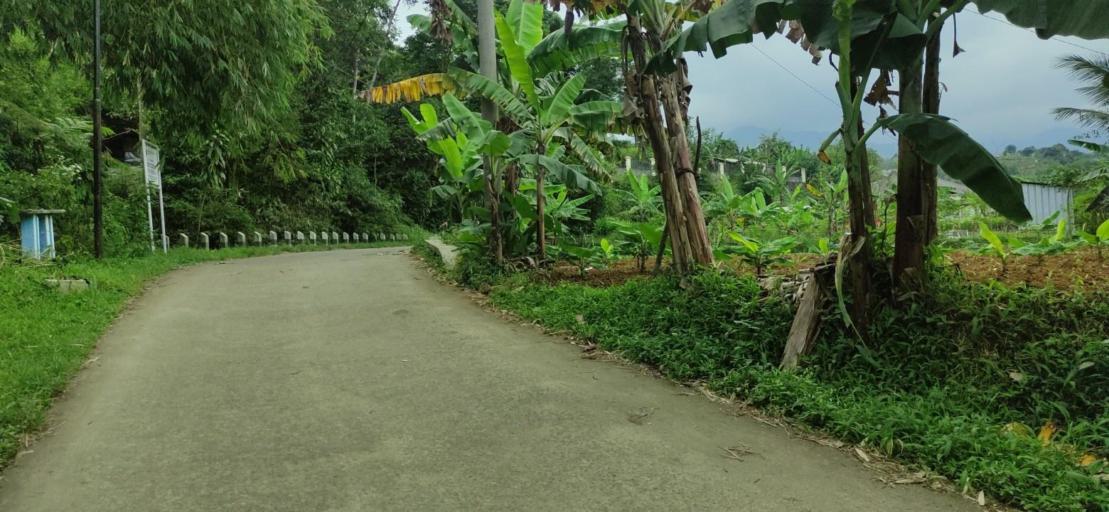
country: ID
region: West Java
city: Caringin
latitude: -6.6435
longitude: 106.8978
